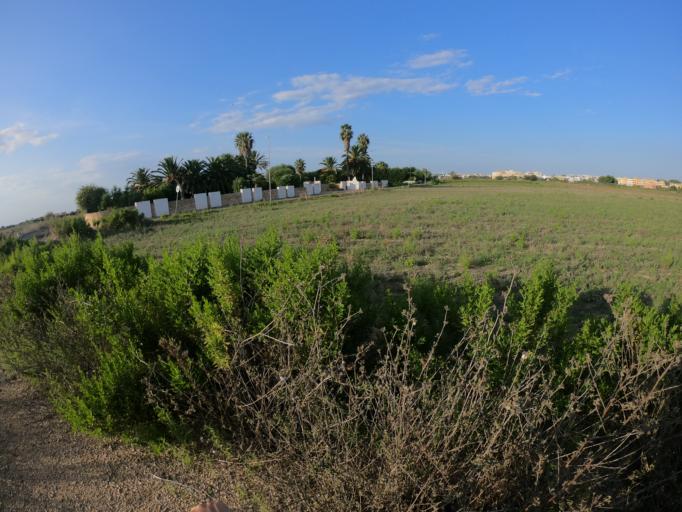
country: IT
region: Apulia
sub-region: Provincia di Lecce
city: Nardo
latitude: 40.1656
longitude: 18.0148
